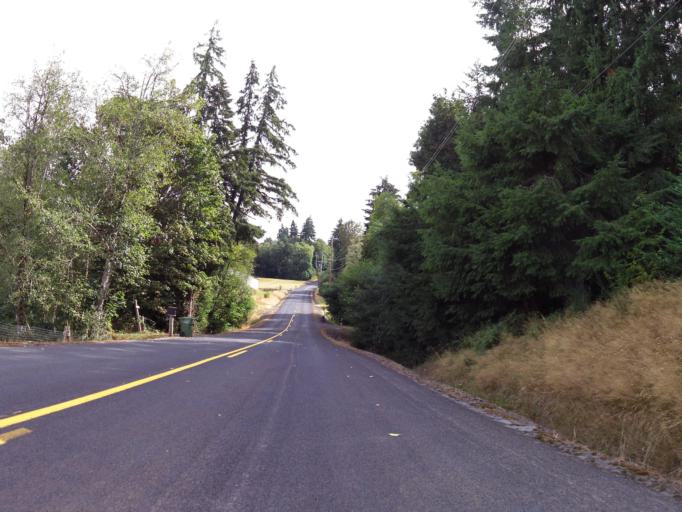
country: US
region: Washington
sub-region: Cowlitz County
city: Castle Rock
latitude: 46.3204
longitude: -122.9260
